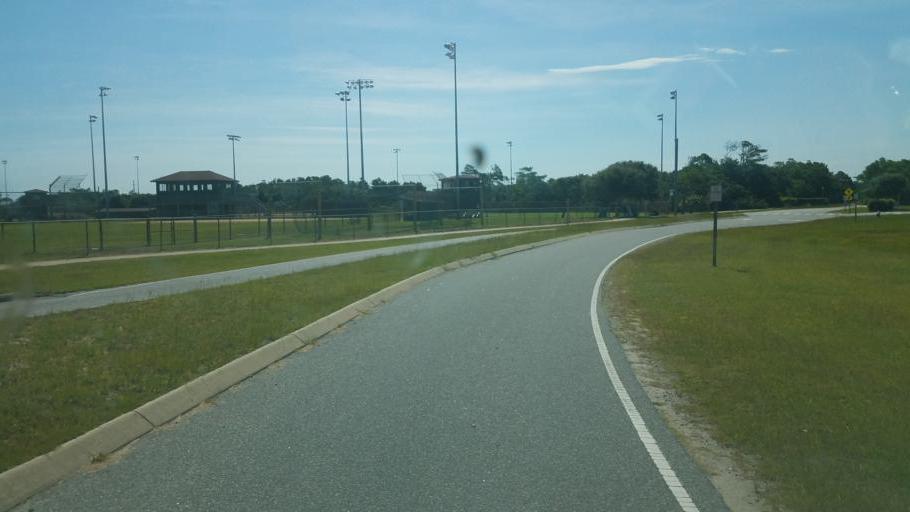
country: US
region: North Carolina
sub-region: Dare County
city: Kill Devil Hills
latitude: 36.0080
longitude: -75.6641
